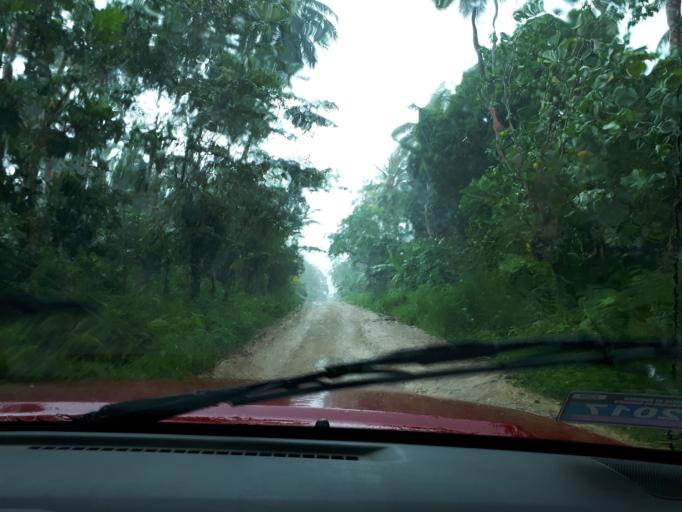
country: VU
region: Sanma
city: Luganville
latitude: -15.5601
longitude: 166.9955
